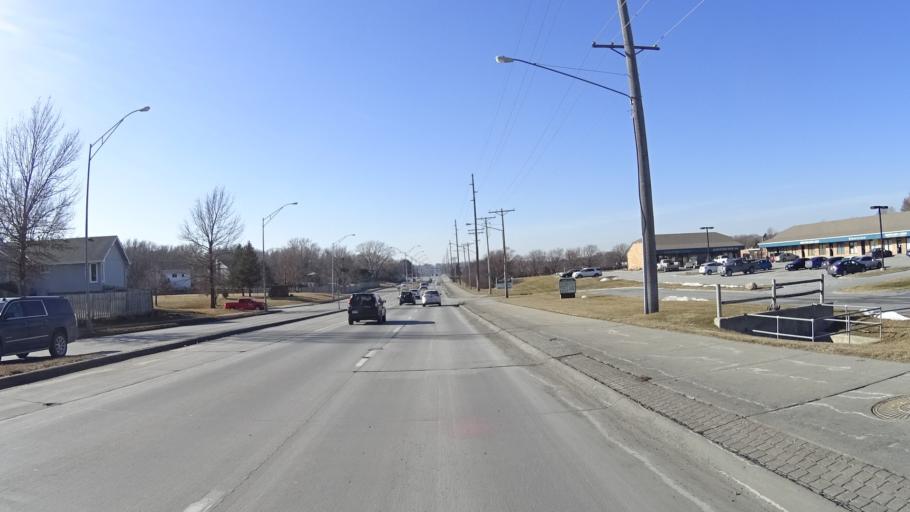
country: US
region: Nebraska
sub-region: Douglas County
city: Bennington
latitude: 41.3067
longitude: -96.0844
